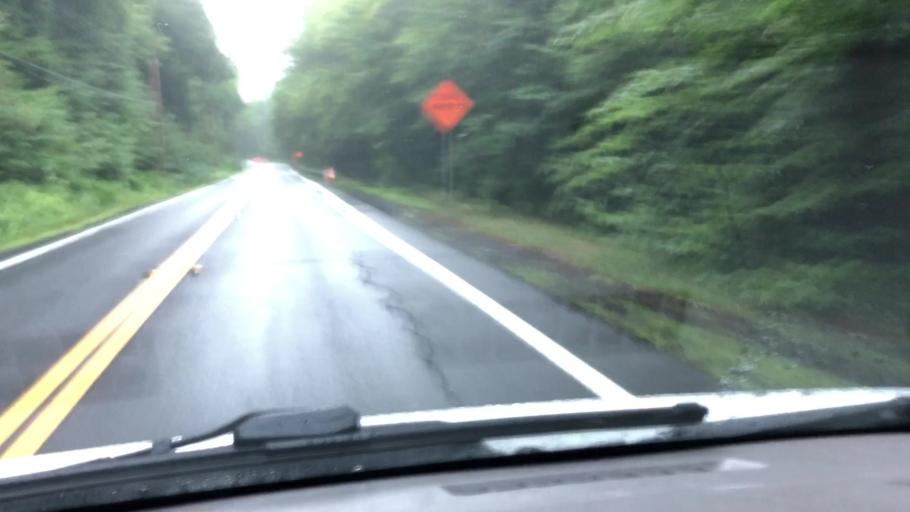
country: US
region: Massachusetts
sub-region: Hampshire County
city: Chesterfield
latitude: 42.3457
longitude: -72.8948
